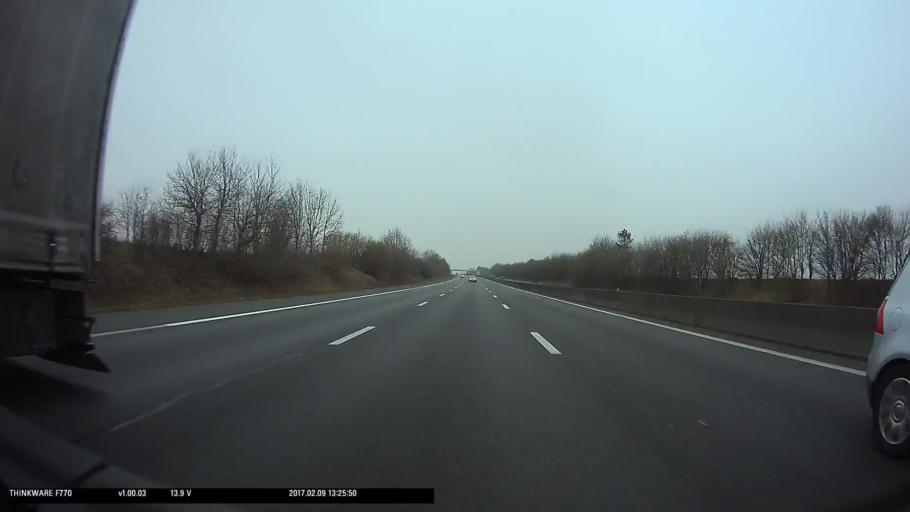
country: FR
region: Centre
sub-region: Departement d'Eure-et-Loir
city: Baigneaux
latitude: 48.1419
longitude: 1.8554
